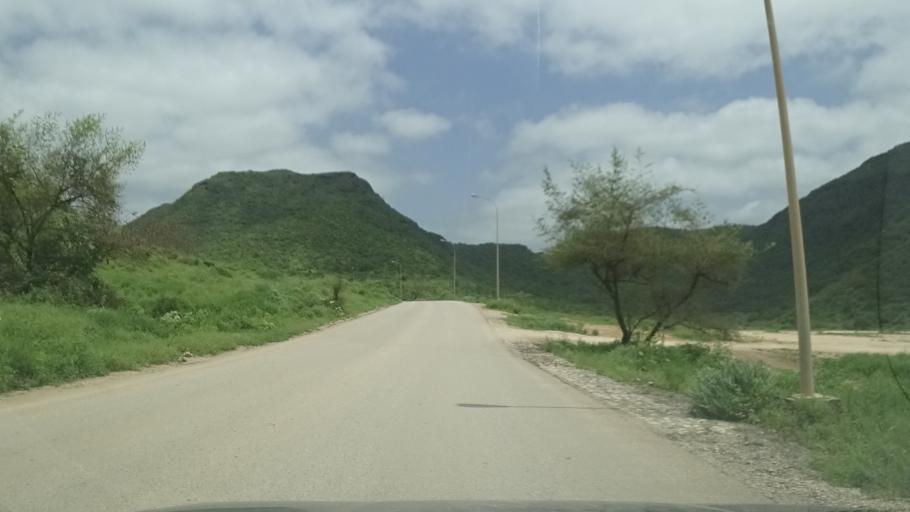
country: OM
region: Zufar
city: Salalah
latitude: 17.1471
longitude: 54.1765
